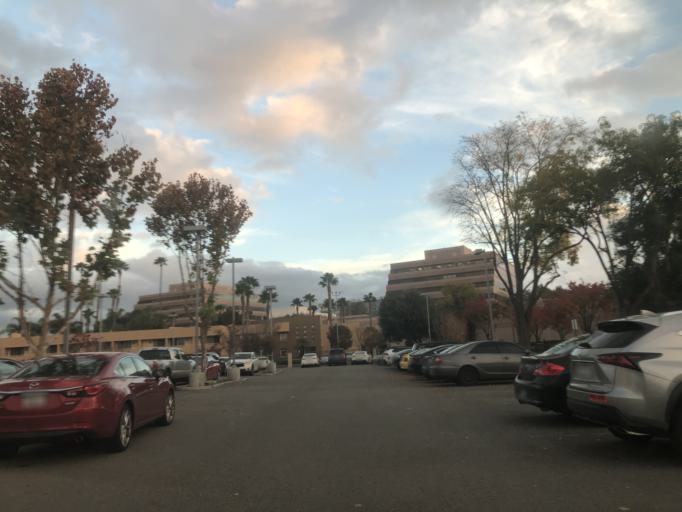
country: US
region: California
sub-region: Santa Clara County
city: San Jose
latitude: 37.3705
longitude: -121.9192
